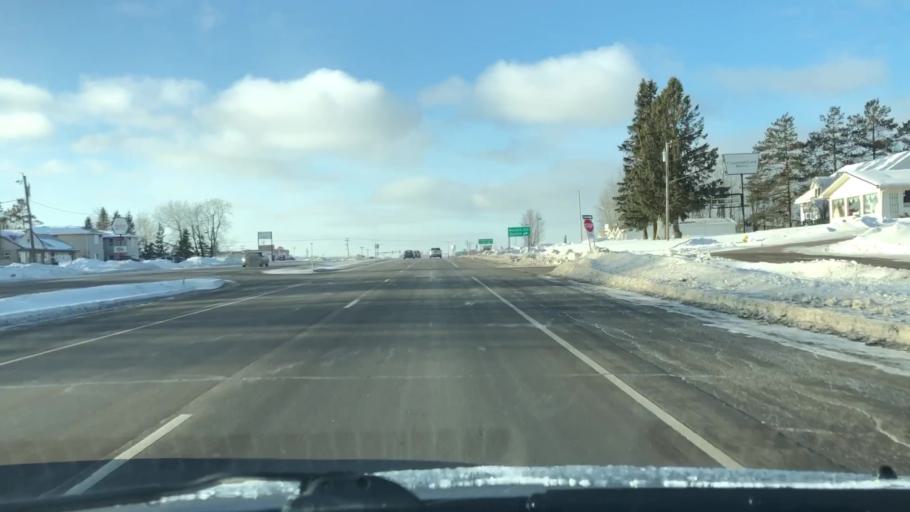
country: US
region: Minnesota
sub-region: Saint Louis County
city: Hermantown
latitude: 46.8250
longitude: -92.1913
